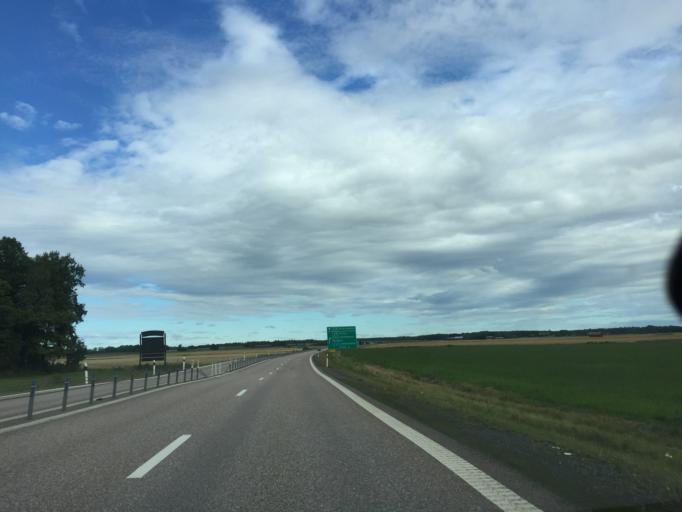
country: SE
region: Vaestmanland
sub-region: Arboga Kommun
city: Arboga
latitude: 59.4193
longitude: 15.8862
